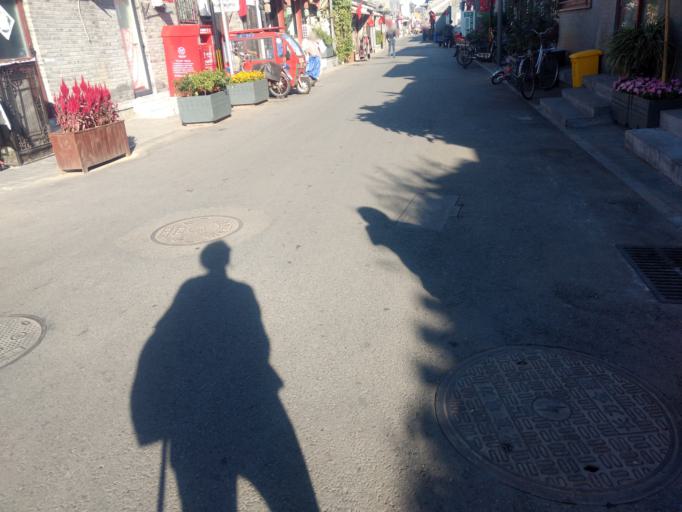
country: CN
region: Beijing
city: Beijing
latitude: 39.8976
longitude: 116.3837
